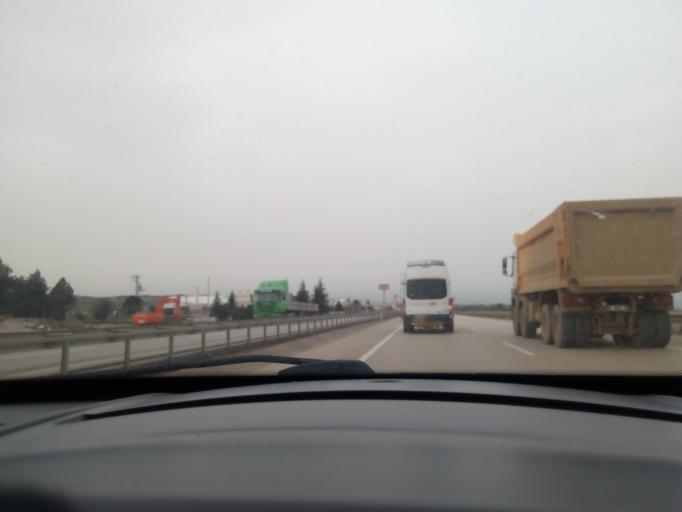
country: TR
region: Bursa
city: Tatkavakli
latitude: 40.0314
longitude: 28.3439
